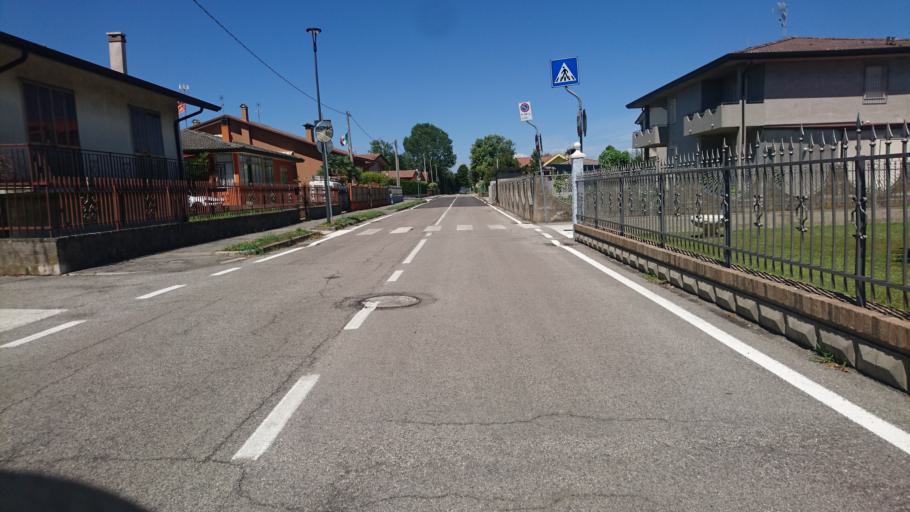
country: IT
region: Veneto
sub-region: Provincia di Padova
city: Campagnola
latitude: 45.2809
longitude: 11.9999
